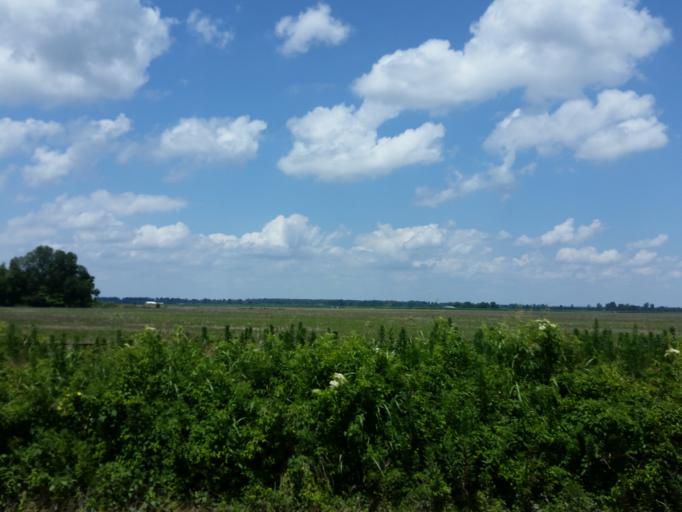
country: US
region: Tennessee
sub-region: Lake County
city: Tiptonville
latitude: 36.4955
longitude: -89.3634
